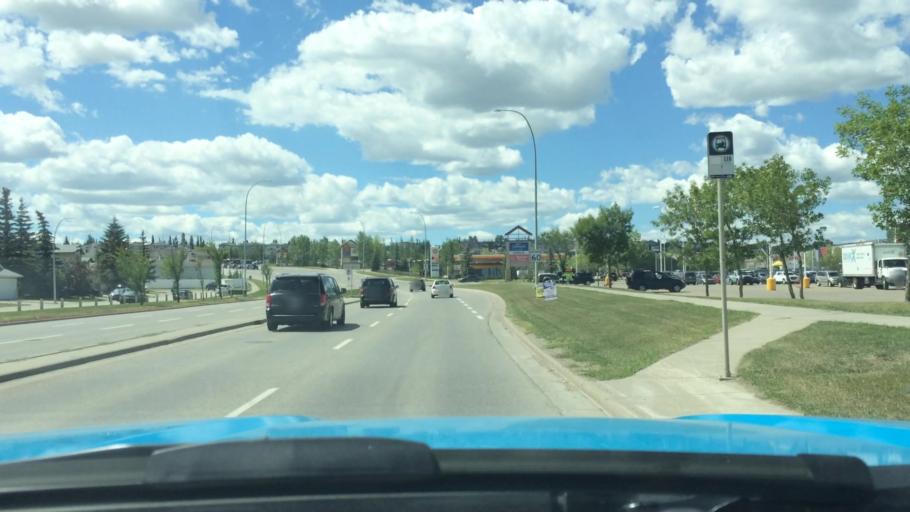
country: CA
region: Alberta
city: Calgary
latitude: 51.1543
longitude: -114.0615
